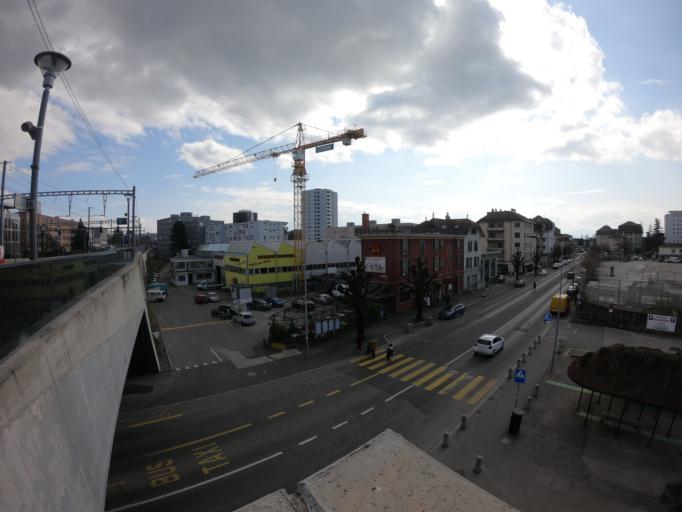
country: CH
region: Vaud
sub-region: Ouest Lausannois District
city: Prilly
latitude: 46.5264
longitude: 6.6030
